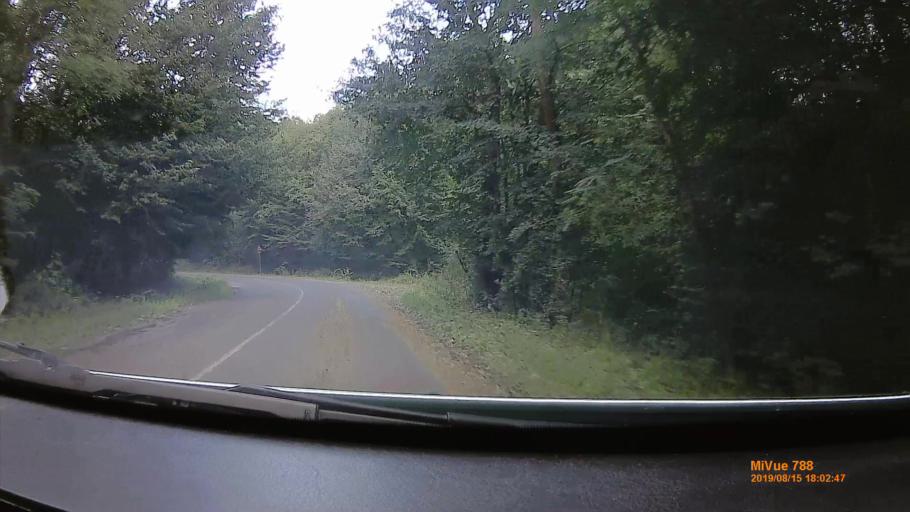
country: HU
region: Borsod-Abauj-Zemplen
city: Sajobabony
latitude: 48.1554
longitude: 20.6539
